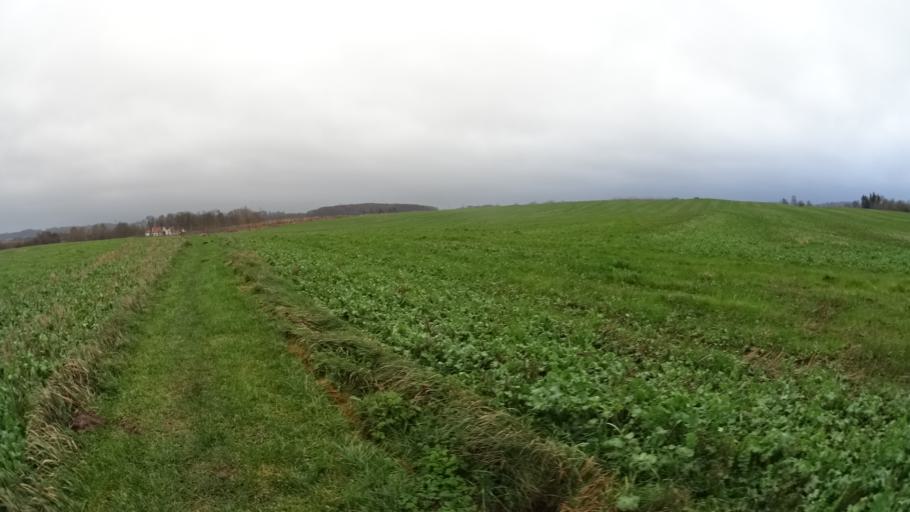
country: DK
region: Central Jutland
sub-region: Arhus Kommune
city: Framlev
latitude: 56.1331
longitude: 10.0245
